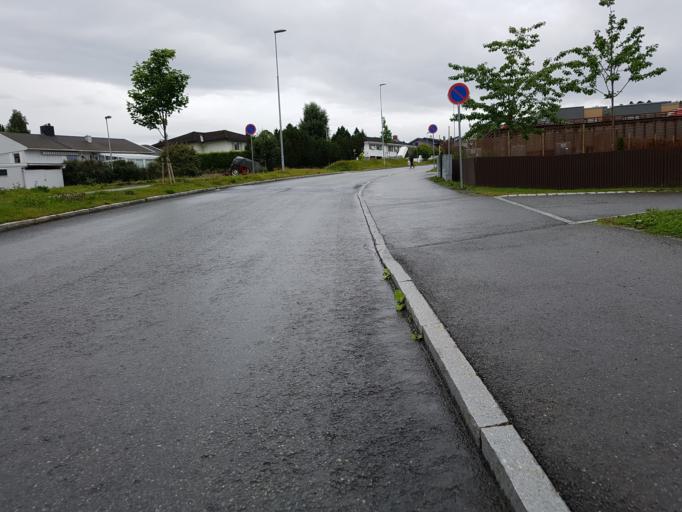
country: NO
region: Sor-Trondelag
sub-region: Trondheim
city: Trondheim
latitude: 63.4130
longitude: 10.4801
